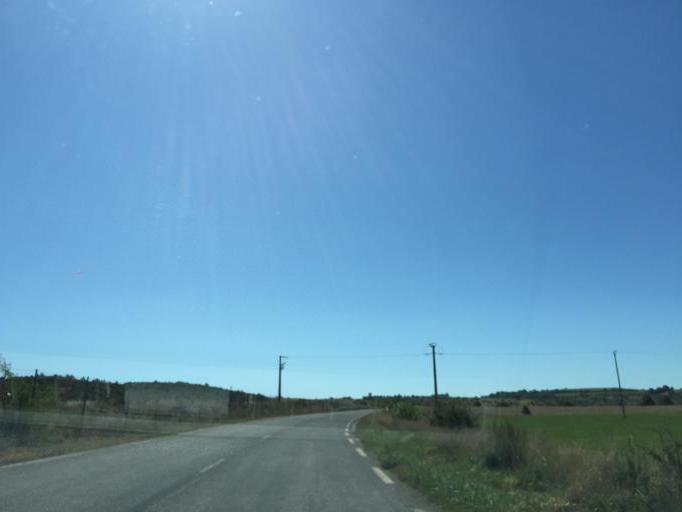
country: FR
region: Midi-Pyrenees
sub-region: Departement de l'Aveyron
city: La Cavalerie
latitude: 43.9167
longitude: 3.2520
